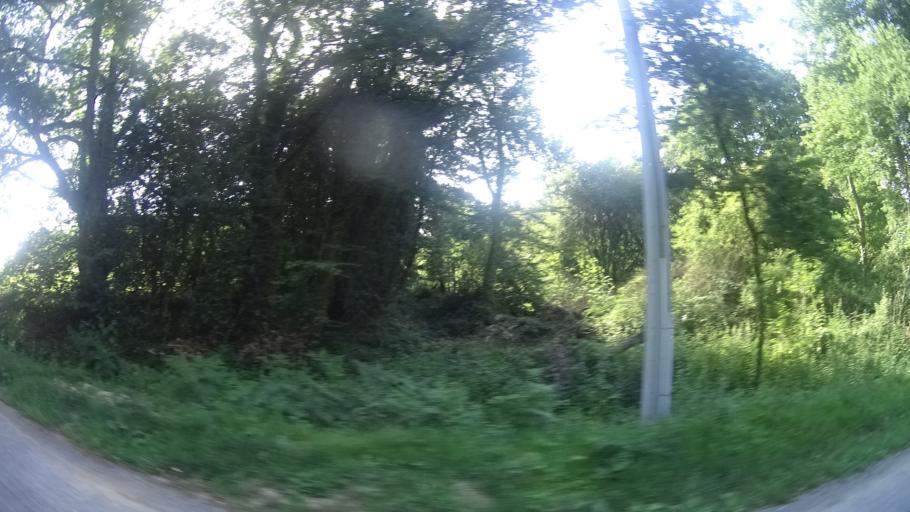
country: FR
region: Brittany
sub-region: Departement du Morbihan
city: Allaire
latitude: 47.6401
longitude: -2.1436
